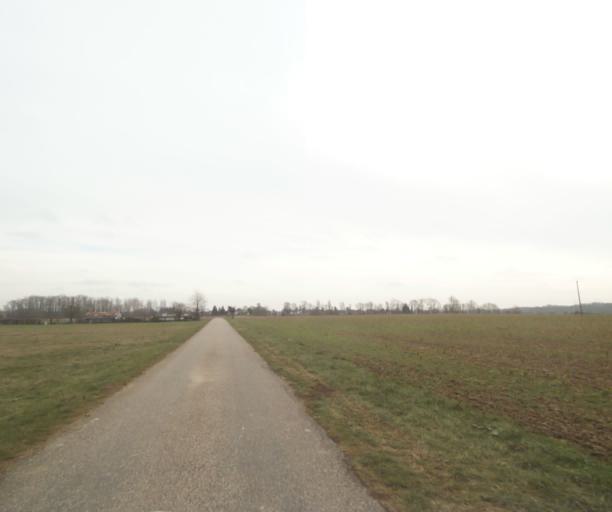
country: FR
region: Champagne-Ardenne
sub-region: Departement de la Haute-Marne
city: Villiers-en-Lieu
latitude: 48.6714
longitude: 4.8859
